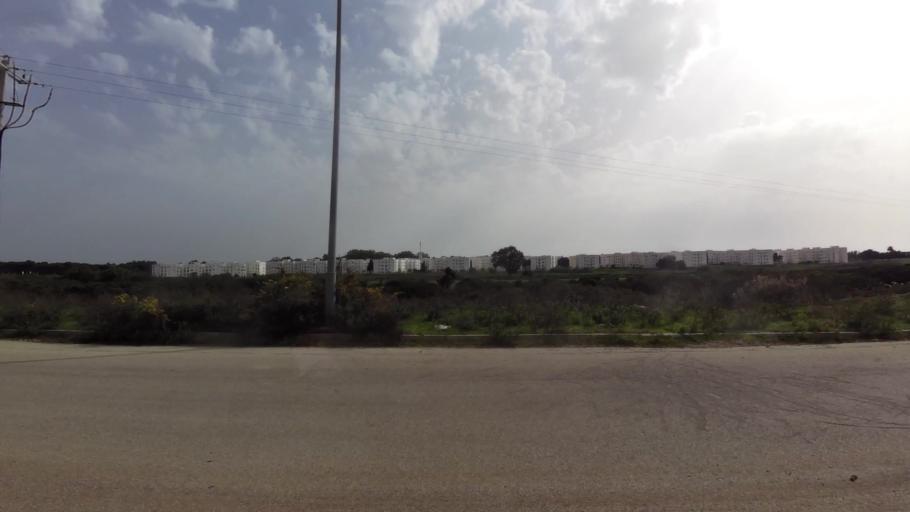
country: MA
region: Tanger-Tetouan
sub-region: Tanger-Assilah
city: Boukhalef
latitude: 35.6882
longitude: -5.9322
